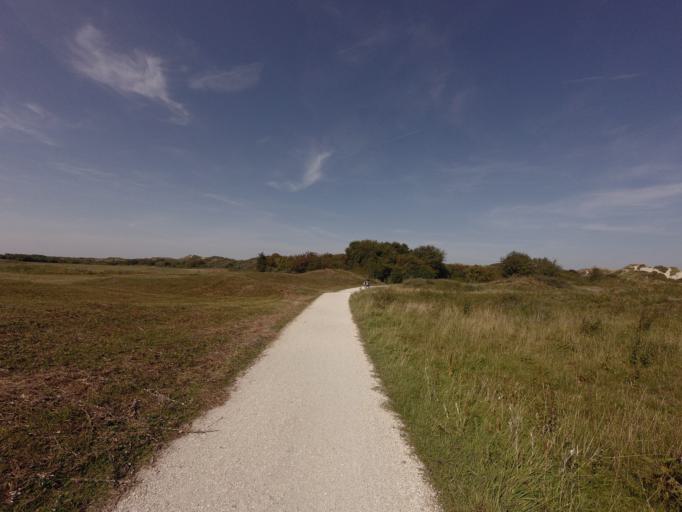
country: NL
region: Friesland
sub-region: Gemeente Schiermonnikoog
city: Schiermonnikoog
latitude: 53.4818
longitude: 6.1464
